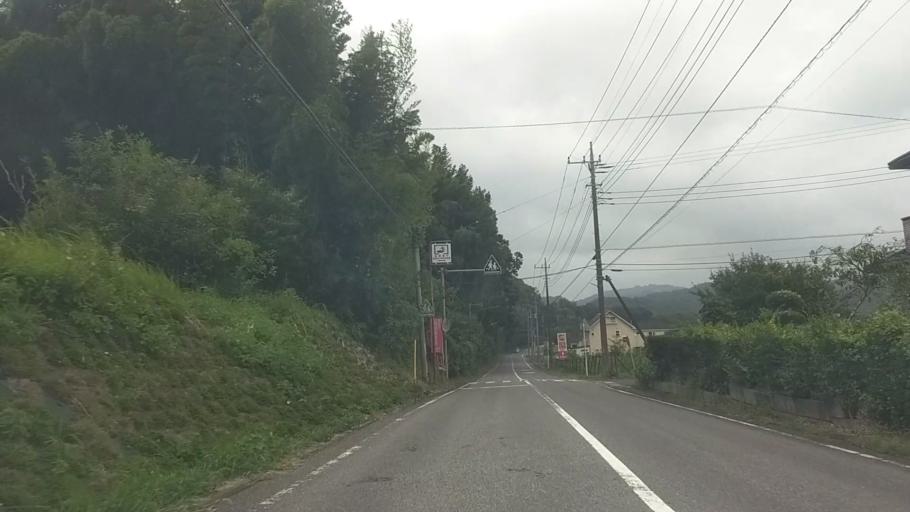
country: JP
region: Chiba
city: Kimitsu
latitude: 35.2347
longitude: 140.0042
